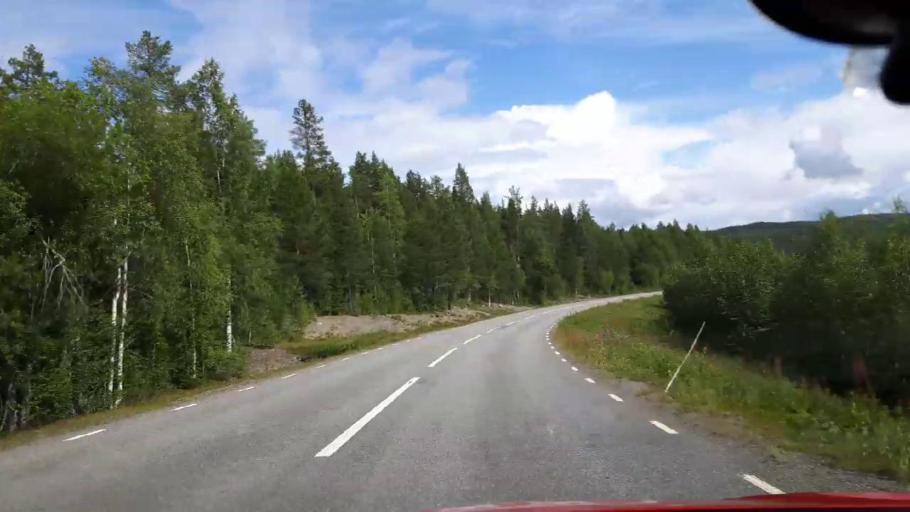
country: SE
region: Jaemtland
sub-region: Stroemsunds Kommun
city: Stroemsund
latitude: 64.3428
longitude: 15.1207
